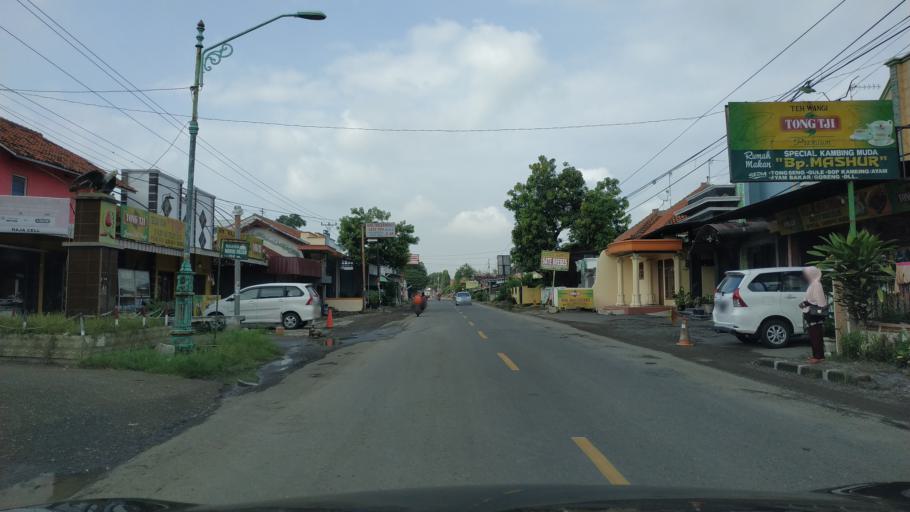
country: ID
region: Central Java
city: Ketanggungan
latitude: -6.8888
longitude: 108.8854
